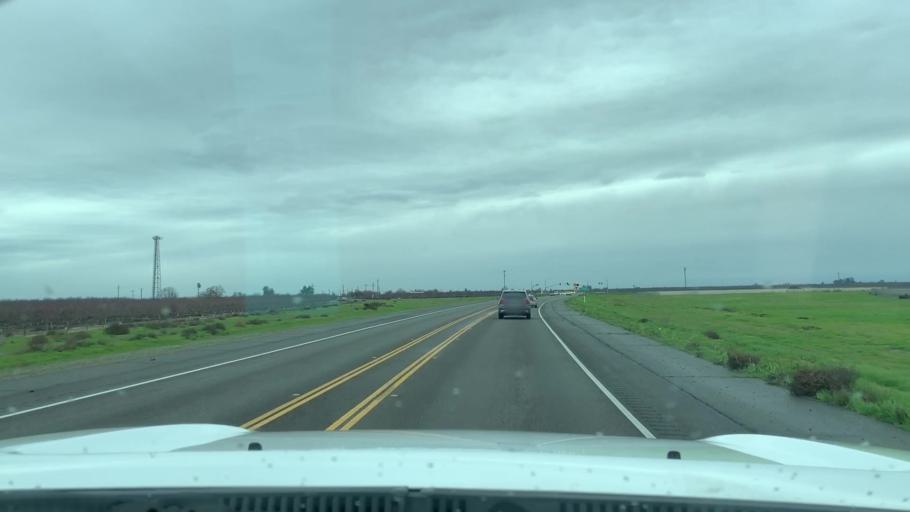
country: US
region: California
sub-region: Fresno County
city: Caruthers
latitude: 36.4849
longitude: -119.7915
